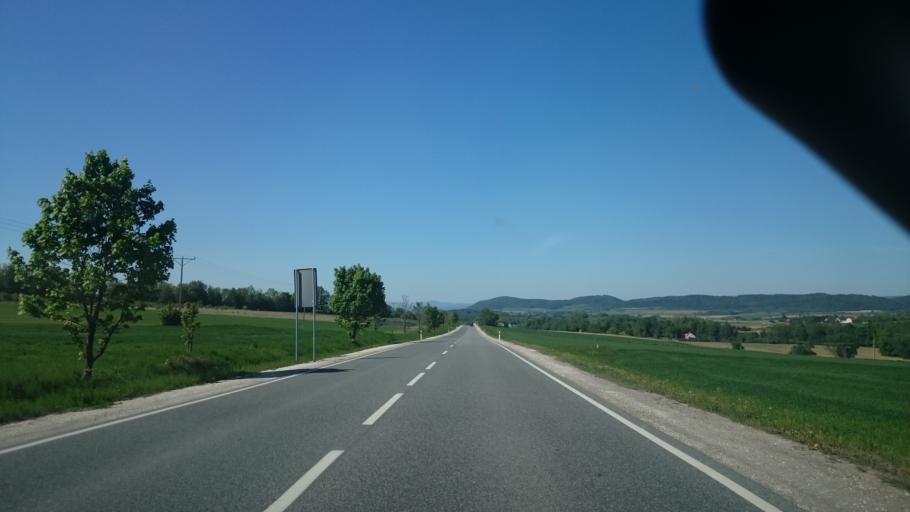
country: PL
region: Lower Silesian Voivodeship
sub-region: Powiat klodzki
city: Bystrzyca Klodzka
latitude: 50.2946
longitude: 16.6627
